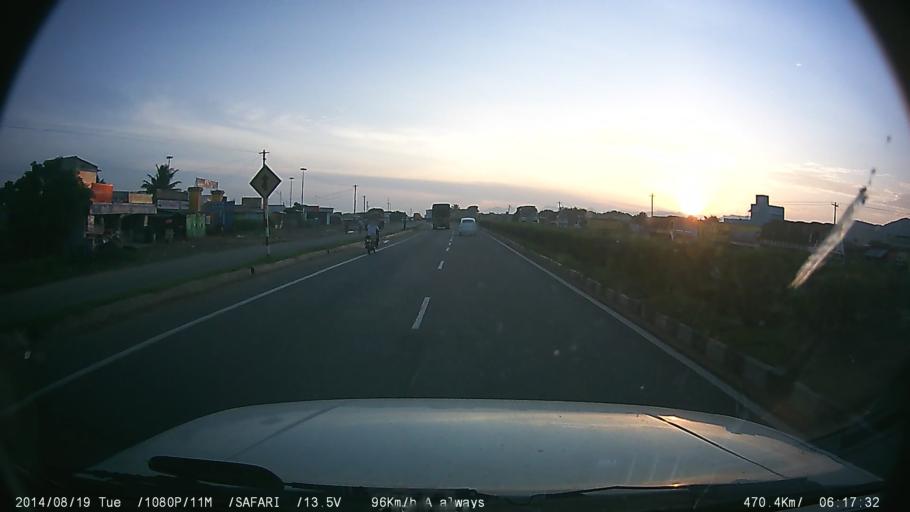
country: IN
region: Tamil Nadu
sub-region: Dharmapuri
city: Dharmapuri
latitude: 11.9963
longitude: 78.0706
